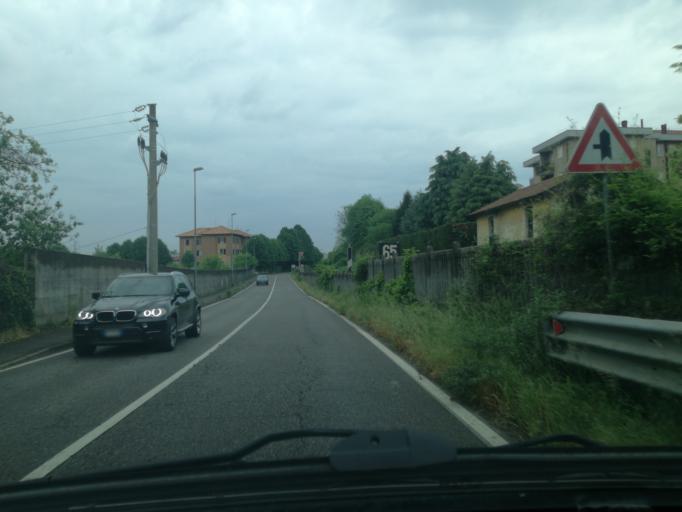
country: IT
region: Lombardy
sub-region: Provincia di Monza e Brianza
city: Triuggio
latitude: 45.6535
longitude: 9.2731
